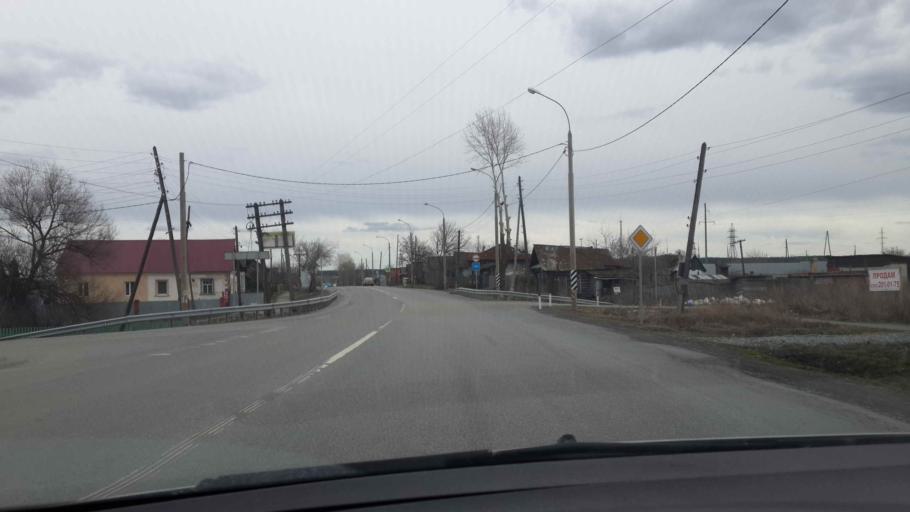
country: RU
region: Sverdlovsk
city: Beloyarskiy
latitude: 56.7569
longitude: 61.3735
